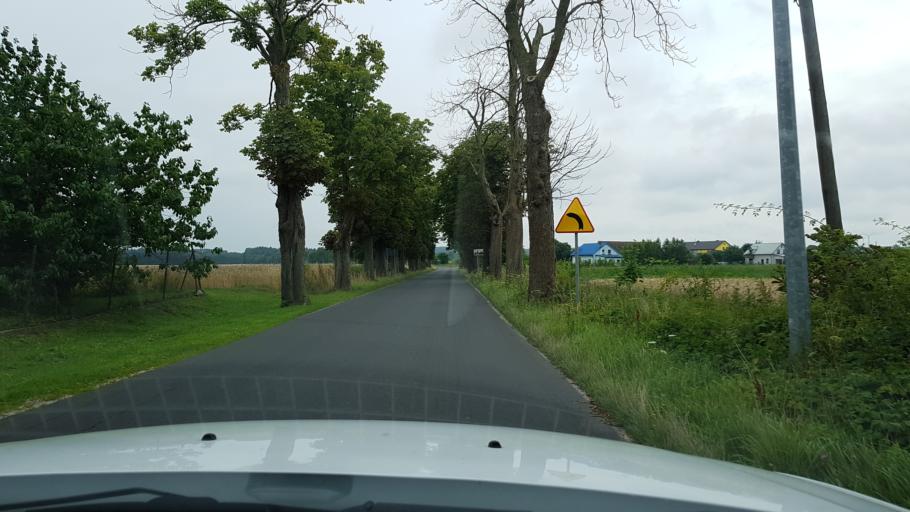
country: PL
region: West Pomeranian Voivodeship
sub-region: Powiat slawienski
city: Slawno
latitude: 54.5065
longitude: 16.5737
